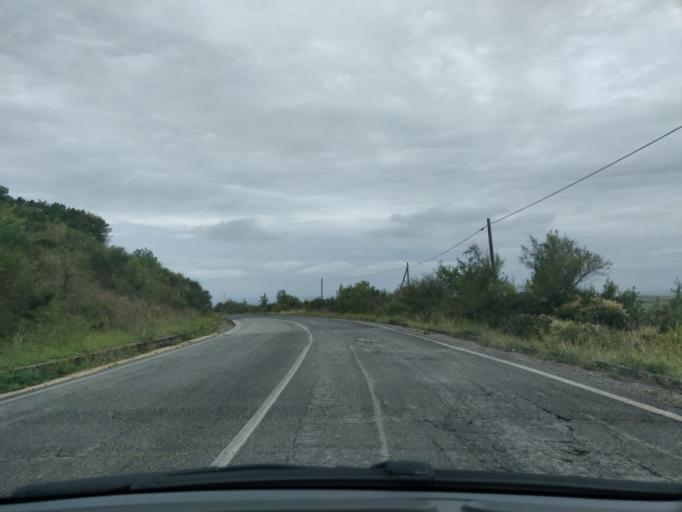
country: IT
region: Latium
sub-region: Citta metropolitana di Roma Capitale
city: Civitavecchia
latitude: 42.1119
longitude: 11.8503
